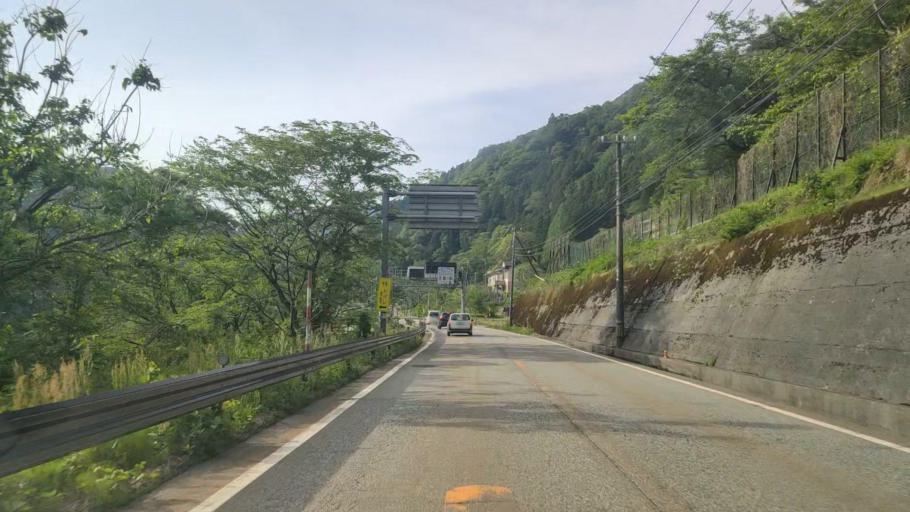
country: JP
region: Toyama
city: Yatsuomachi-higashikumisaka
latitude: 36.4309
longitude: 137.2787
